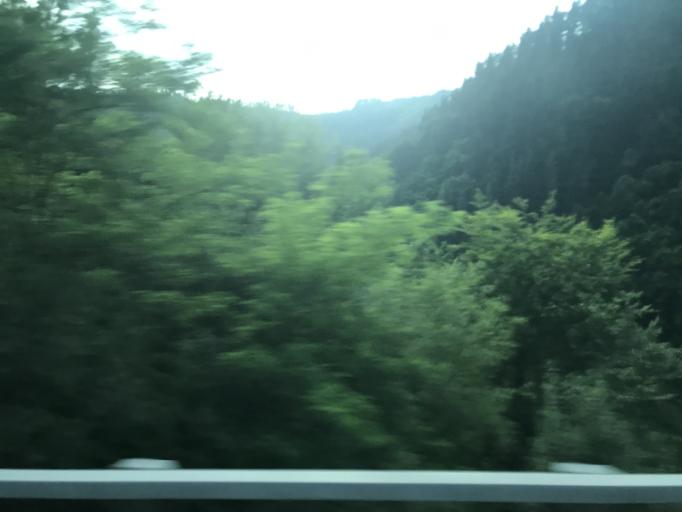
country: ES
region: Basque Country
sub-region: Provincia de Guipuzcoa
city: Elgoibar
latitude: 43.1716
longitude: -2.4254
